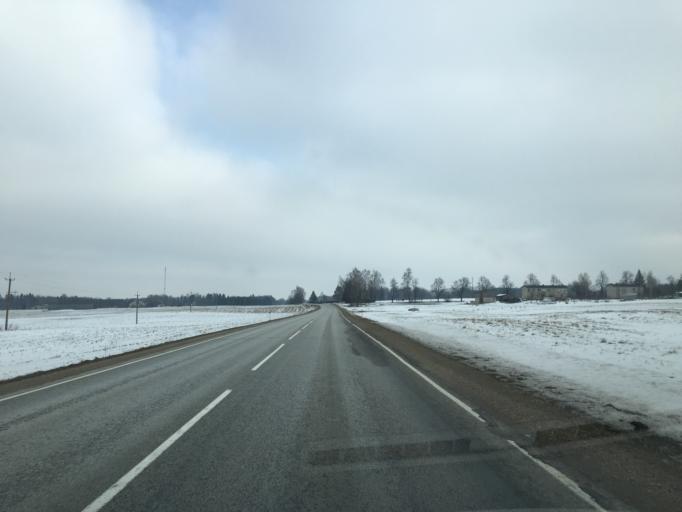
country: EE
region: Tartu
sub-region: Elva linn
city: Elva
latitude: 58.1211
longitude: 26.2415
